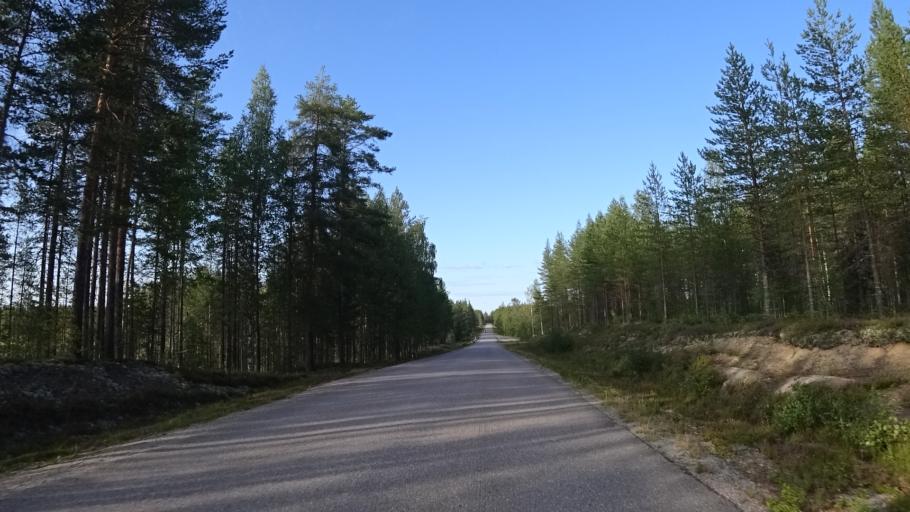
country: FI
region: North Karelia
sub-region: Joensuu
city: Eno
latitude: 63.0772
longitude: 30.5788
